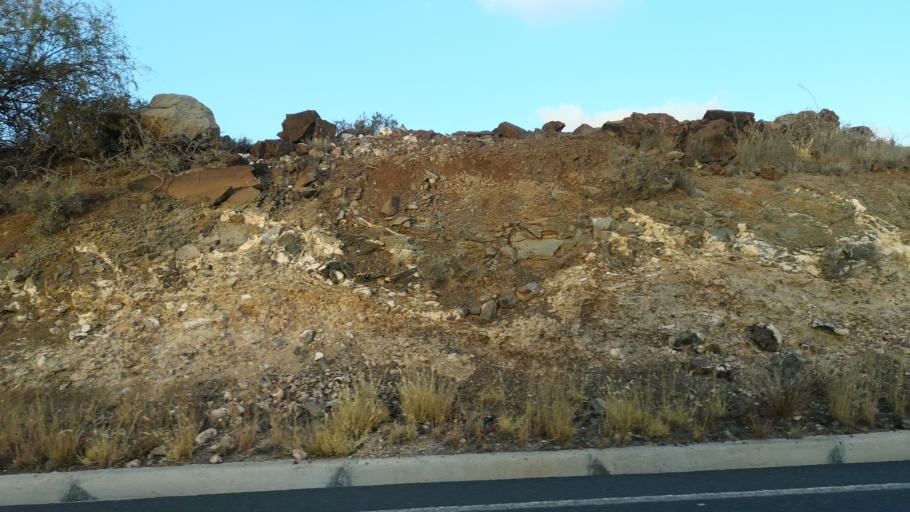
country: ES
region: Canary Islands
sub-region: Provincia de Santa Cruz de Tenerife
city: Alajero
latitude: 28.0330
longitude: -17.2199
